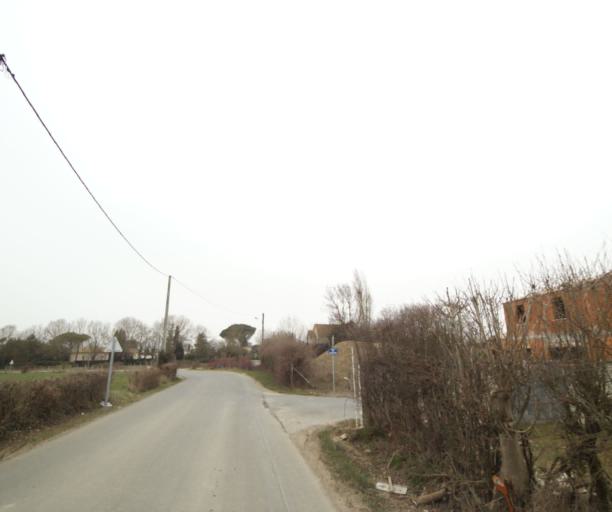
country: FR
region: Poitou-Charentes
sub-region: Departement des Deux-Sevres
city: Bessines
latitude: 46.2964
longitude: -0.4953
